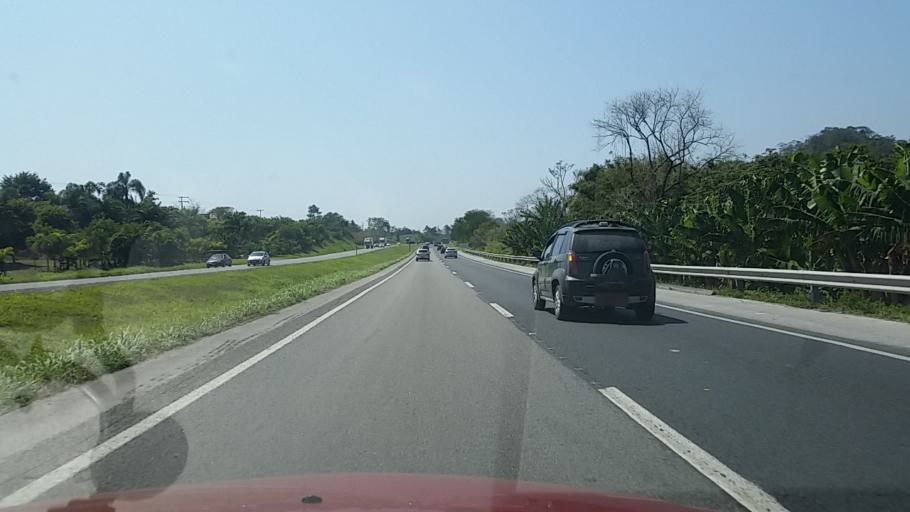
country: BR
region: Sao Paulo
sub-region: Miracatu
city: Miracatu
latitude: -24.2824
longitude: -47.4332
